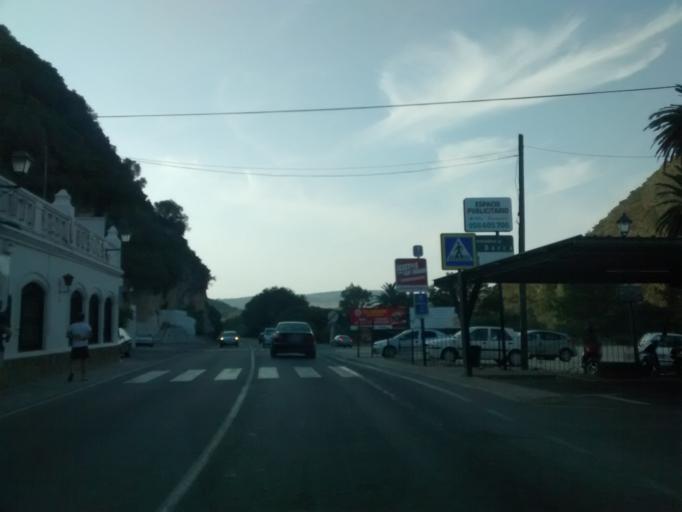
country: ES
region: Andalusia
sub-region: Provincia de Cadiz
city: Vejer de la Frontera
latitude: 36.2534
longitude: -5.9567
